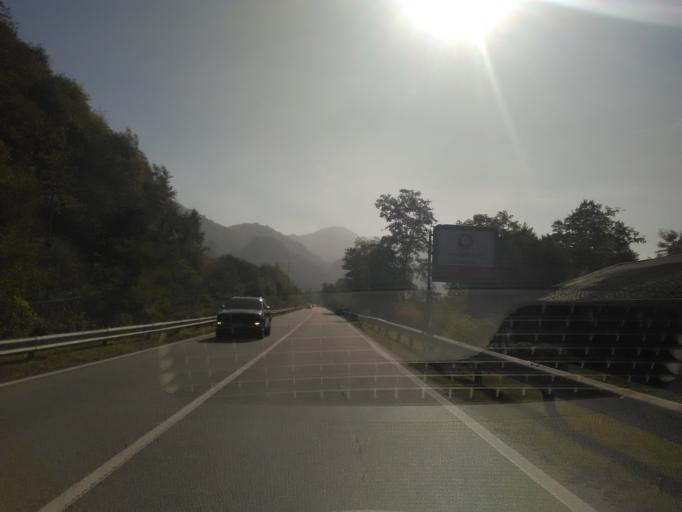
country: IT
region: Piedmont
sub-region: Provincia di Vercelli
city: Varallo
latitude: 45.7992
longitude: 8.2675
